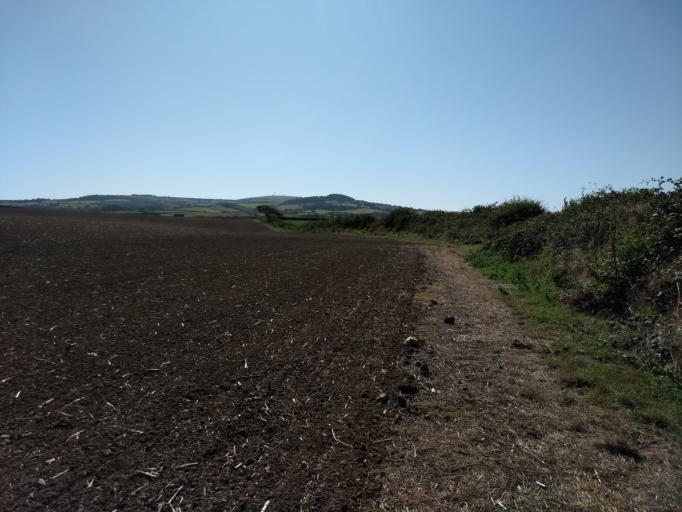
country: GB
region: England
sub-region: Isle of Wight
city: Niton
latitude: 50.6313
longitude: -1.2805
